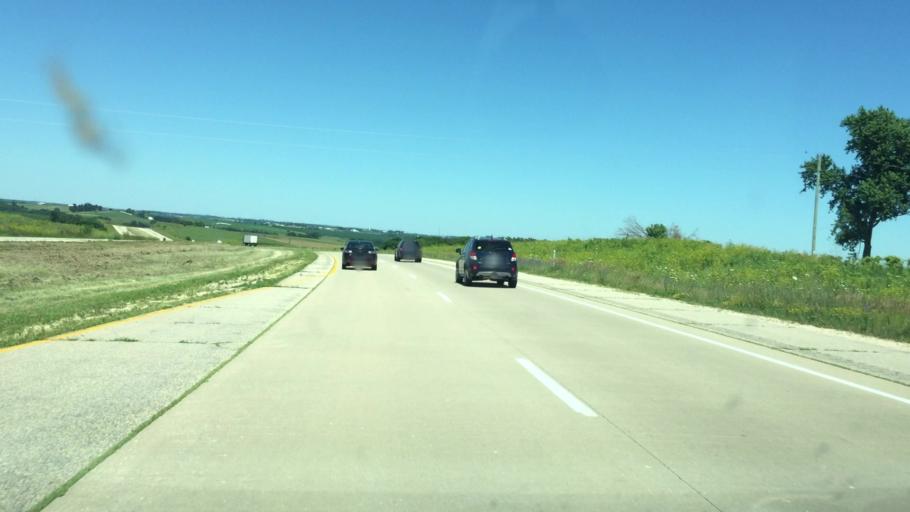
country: US
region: Wisconsin
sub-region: Iowa County
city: Mineral Point
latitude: 42.7963
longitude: -90.2812
